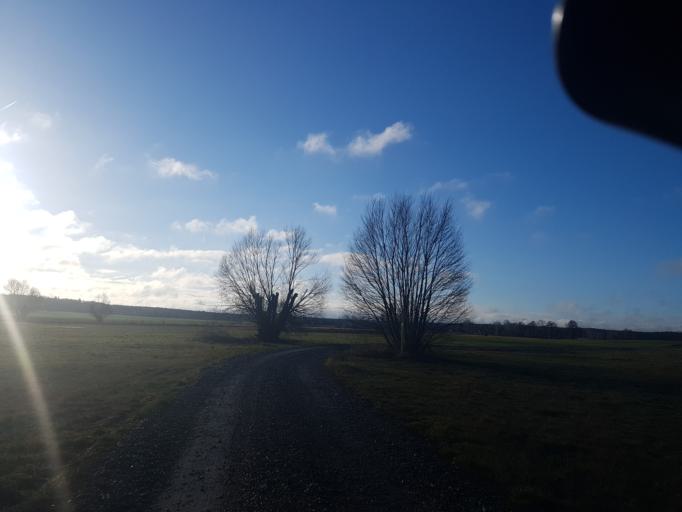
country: DE
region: Brandenburg
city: Schonborn
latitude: 51.5545
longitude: 13.4722
